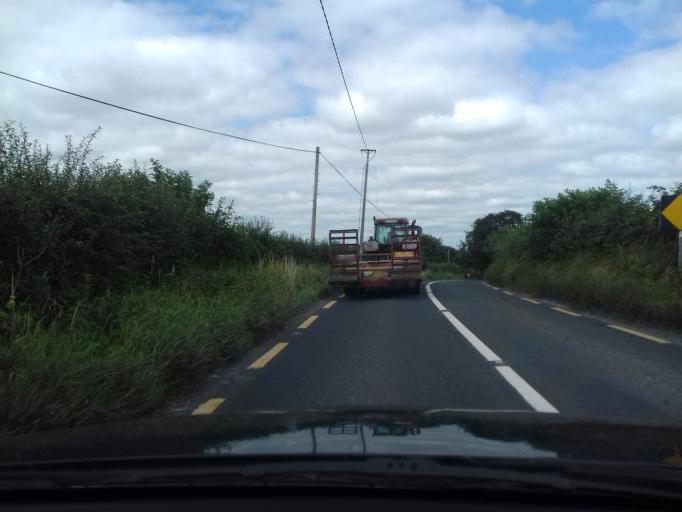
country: IE
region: Leinster
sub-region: County Carlow
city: Tullow
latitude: 52.8275
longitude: -6.7212
